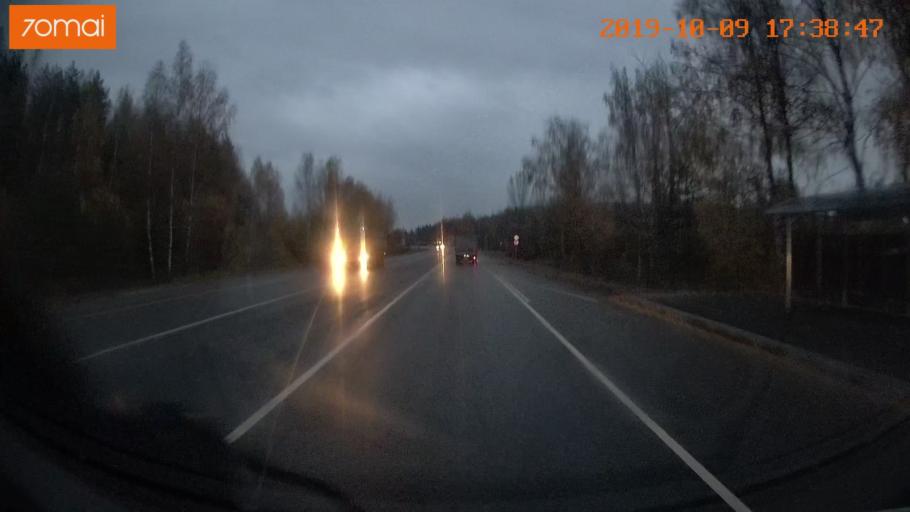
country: RU
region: Ivanovo
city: Bogorodskoye
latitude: 57.0672
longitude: 40.9522
